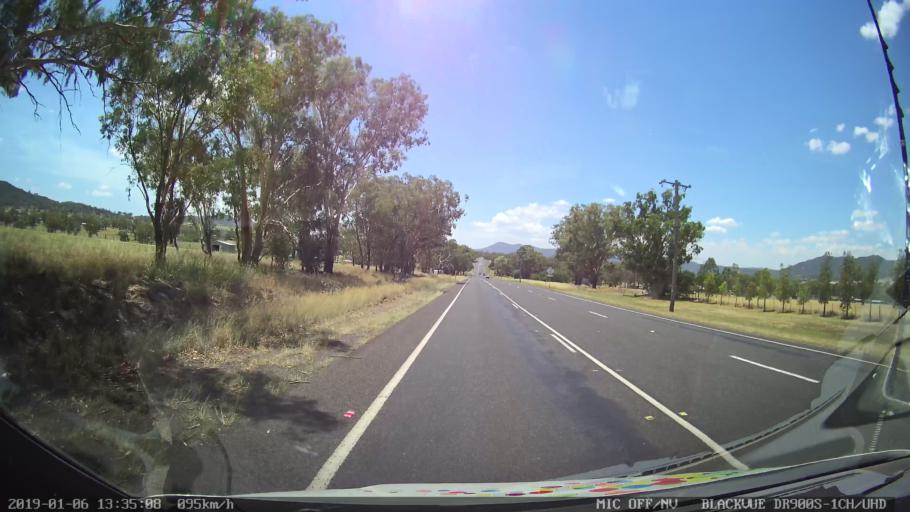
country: AU
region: New South Wales
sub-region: Tamworth Municipality
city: Kootingal
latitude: -31.0807
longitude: 151.0224
